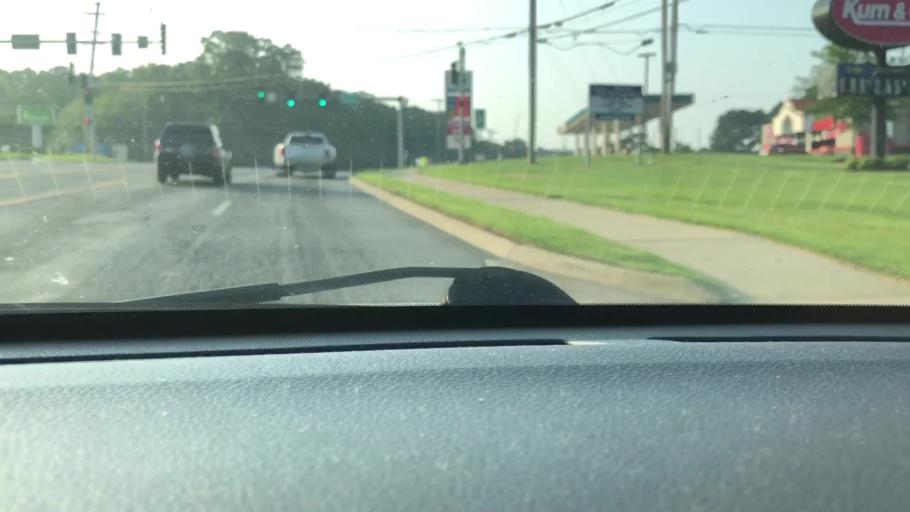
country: US
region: Arkansas
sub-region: Saline County
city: Bryant
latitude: 34.6103
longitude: -92.4939
